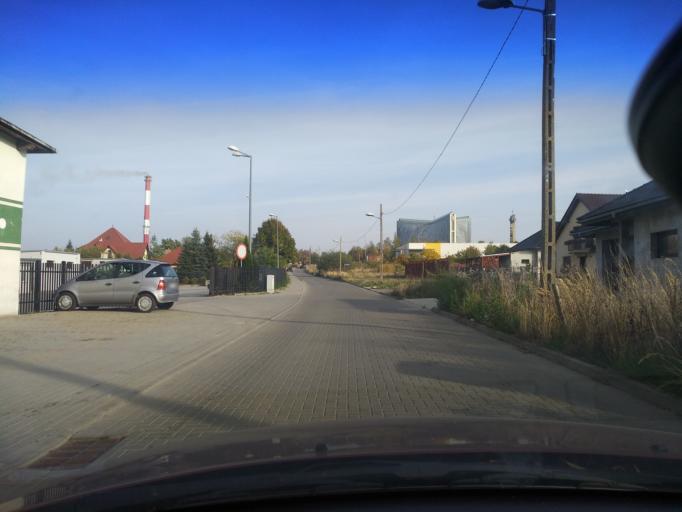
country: PL
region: Lower Silesian Voivodeship
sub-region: Powiat zgorzelecki
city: Zgorzelec
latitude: 51.1623
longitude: 15.0050
